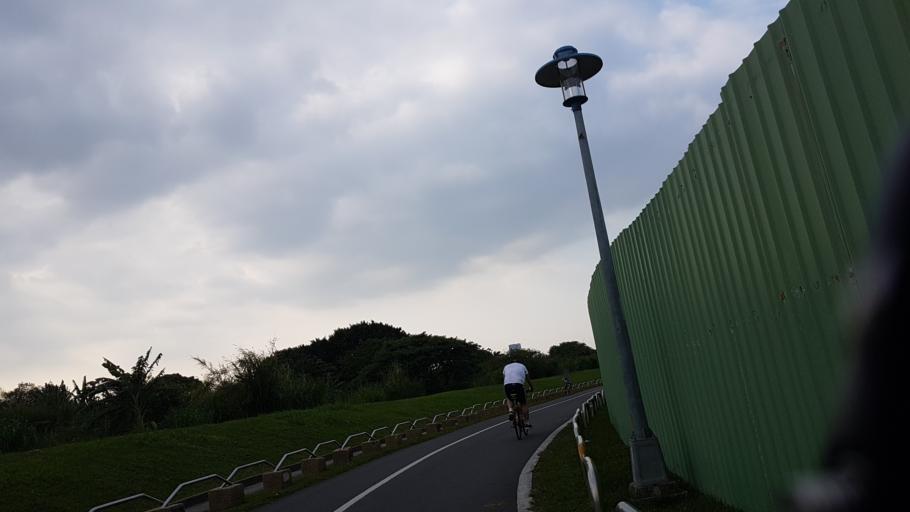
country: TW
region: Taipei
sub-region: Taipei
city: Banqiao
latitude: 25.0320
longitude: 121.4866
